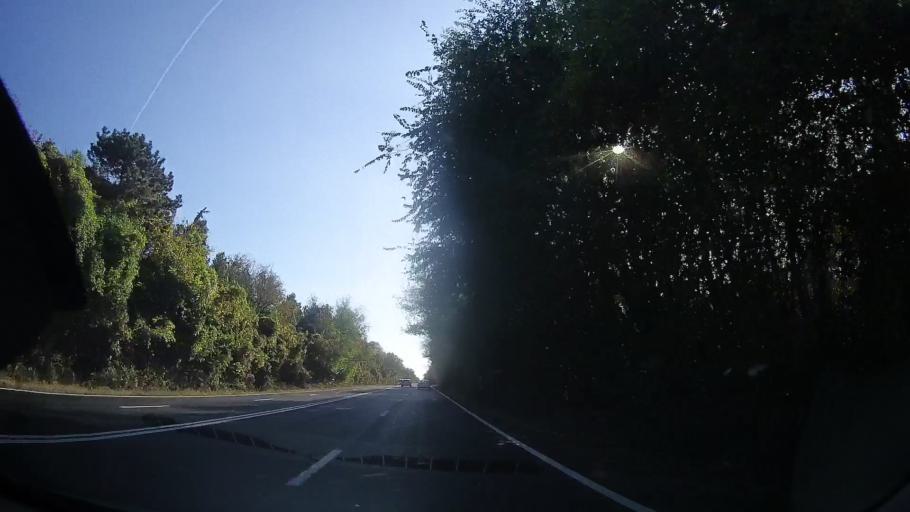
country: RO
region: Constanta
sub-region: Comuna Douazeci si Trei August
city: Dulcesti
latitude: 43.8706
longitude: 28.5745
